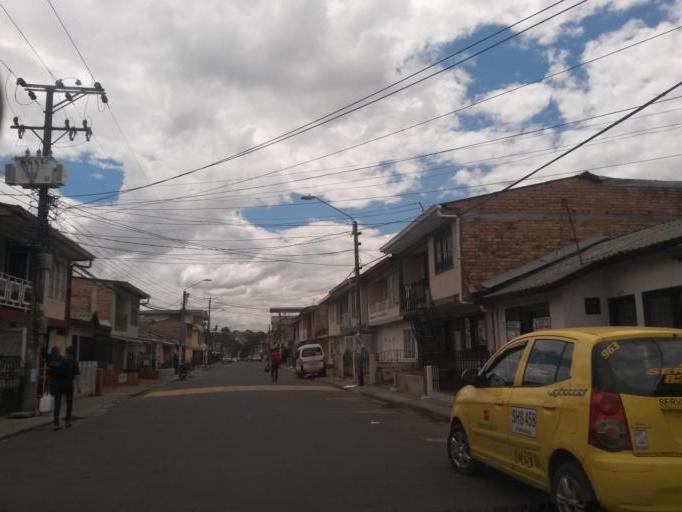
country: CO
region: Cauca
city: Popayan
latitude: 2.4481
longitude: -76.6235
